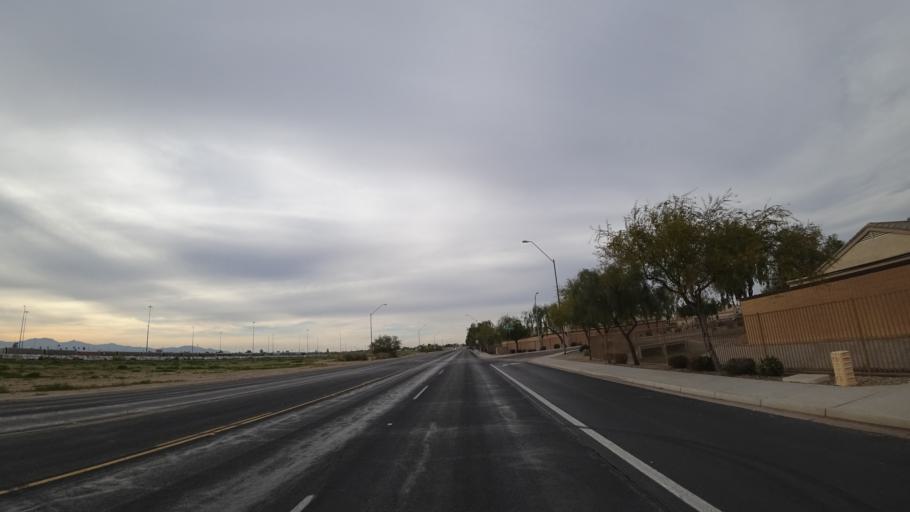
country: US
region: Arizona
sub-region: Maricopa County
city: El Mirage
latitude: 33.6182
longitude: -112.3162
